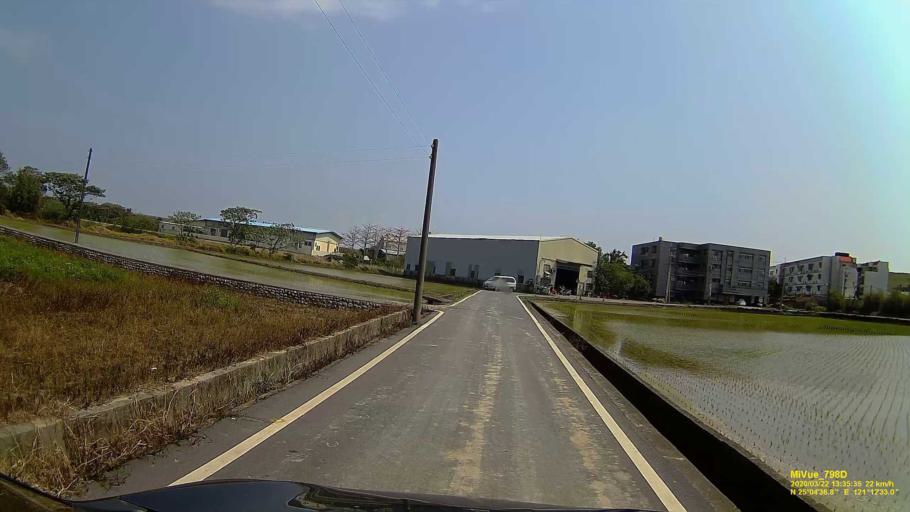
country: TW
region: Taiwan
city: Taoyuan City
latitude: 25.0768
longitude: 121.2092
